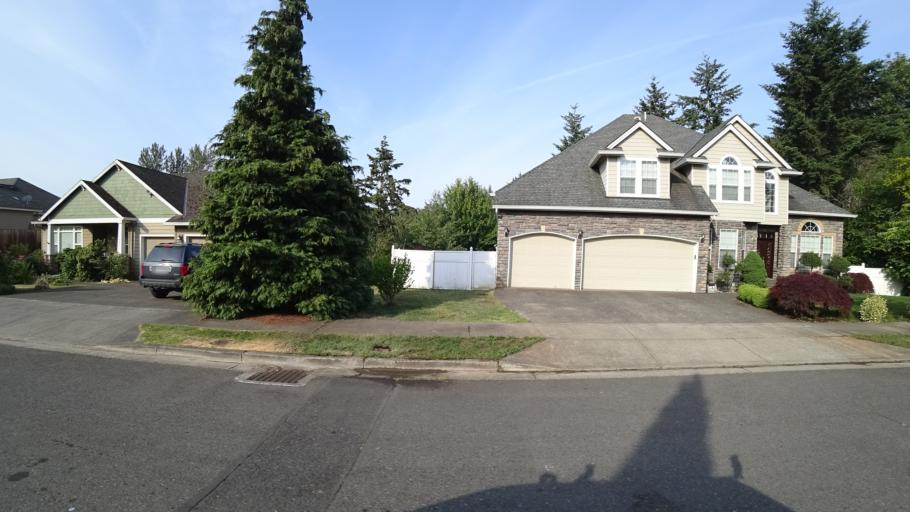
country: US
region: Oregon
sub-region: Clackamas County
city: Happy Valley
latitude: 45.4629
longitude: -122.5274
